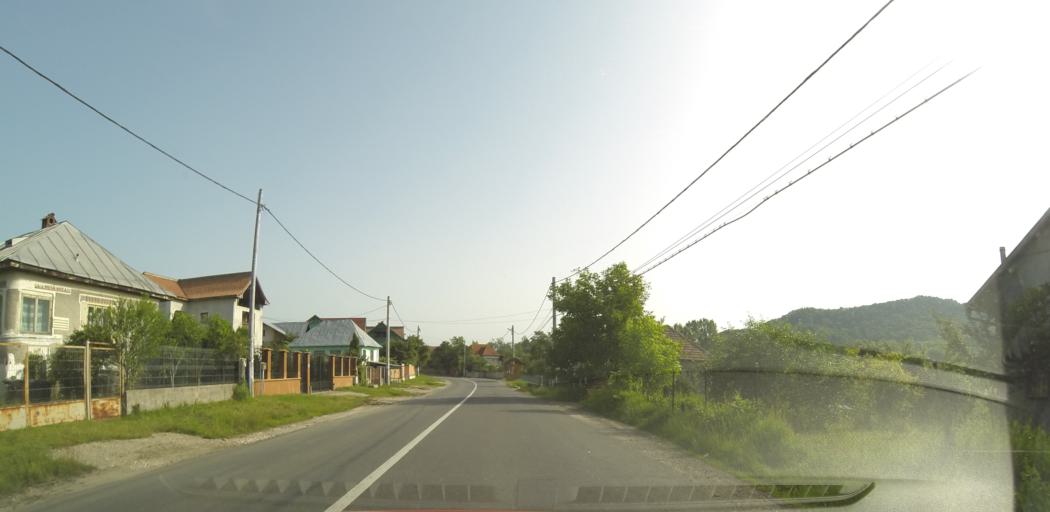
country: RO
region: Valcea
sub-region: Comuna Pausesti-Maglasi
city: Pausesti-Maglasi
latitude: 45.1458
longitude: 24.2456
